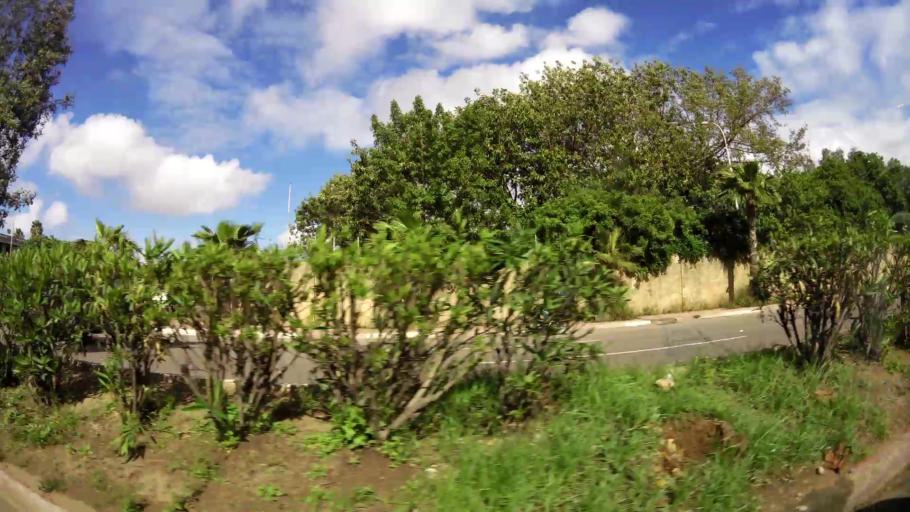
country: MA
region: Grand Casablanca
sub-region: Casablanca
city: Casablanca
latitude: 33.5410
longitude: -7.6184
